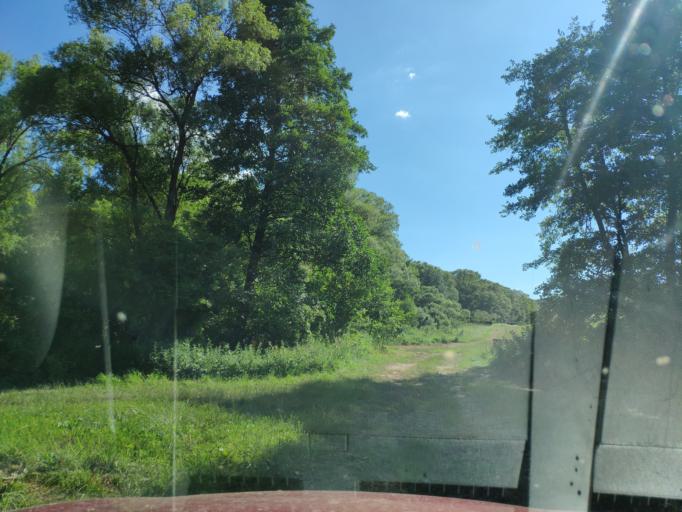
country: SK
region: Banskobystricky
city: Rimavska Sobota
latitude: 48.2592
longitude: 20.1139
